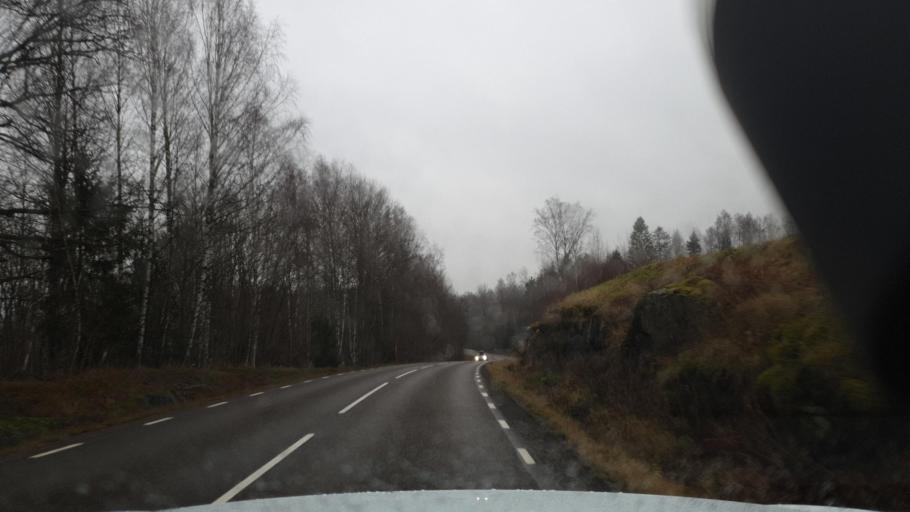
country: SE
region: Vaermland
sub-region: Eda Kommun
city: Amotfors
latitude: 59.7218
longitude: 12.4270
